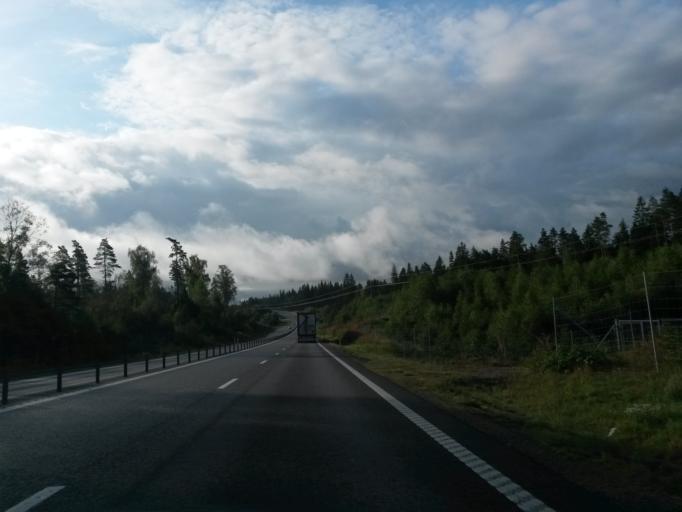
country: SE
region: Vaestra Goetaland
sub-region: Boras Kommun
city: Dalsjofors
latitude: 57.6427
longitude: 13.0702
